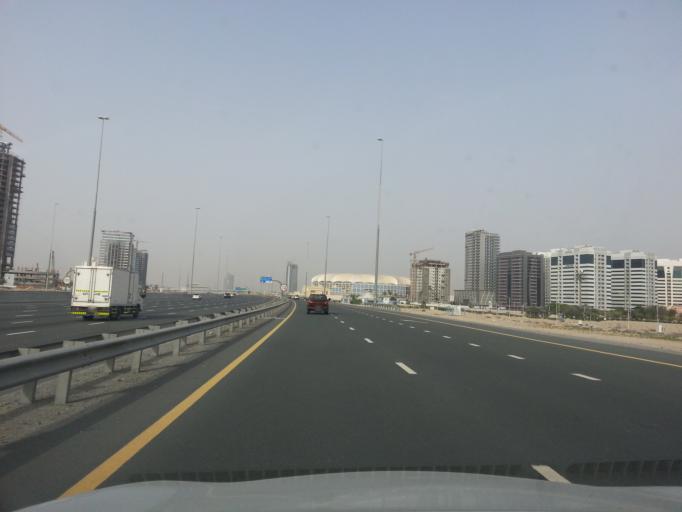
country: AE
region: Dubai
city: Dubai
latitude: 25.0447
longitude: 55.2081
